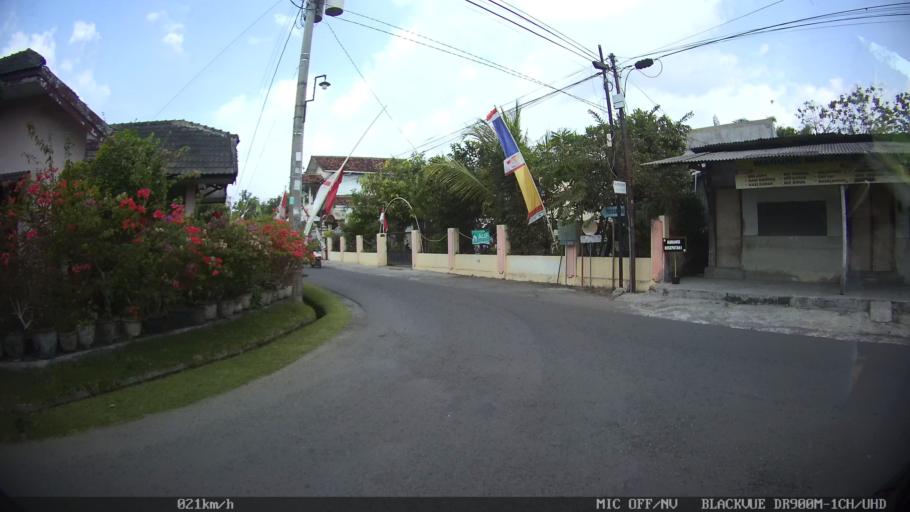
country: ID
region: Daerah Istimewa Yogyakarta
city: Yogyakarta
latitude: -7.8057
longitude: 110.4054
